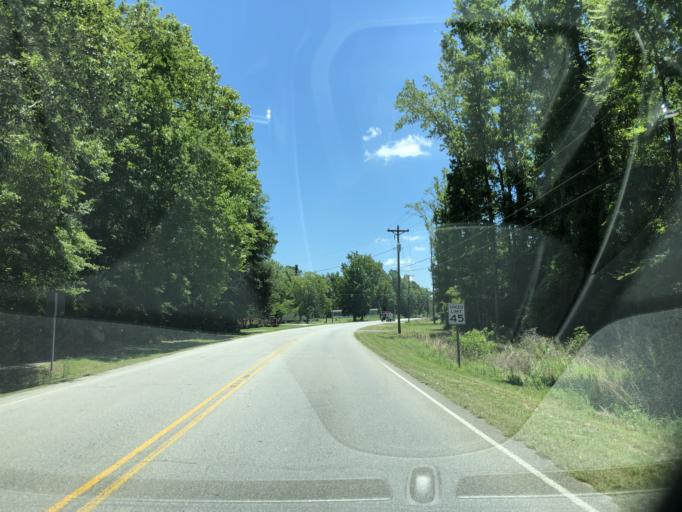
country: US
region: South Carolina
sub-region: Orangeburg County
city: Branchville
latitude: 33.2515
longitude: -80.8100
